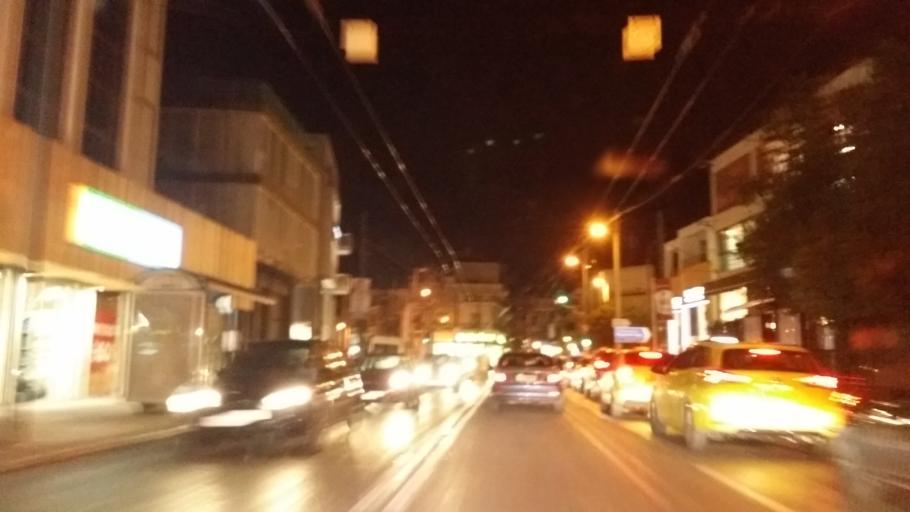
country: GR
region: Attica
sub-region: Nomarchia Athinas
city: Khalandrion
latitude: 38.0174
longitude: 23.7952
